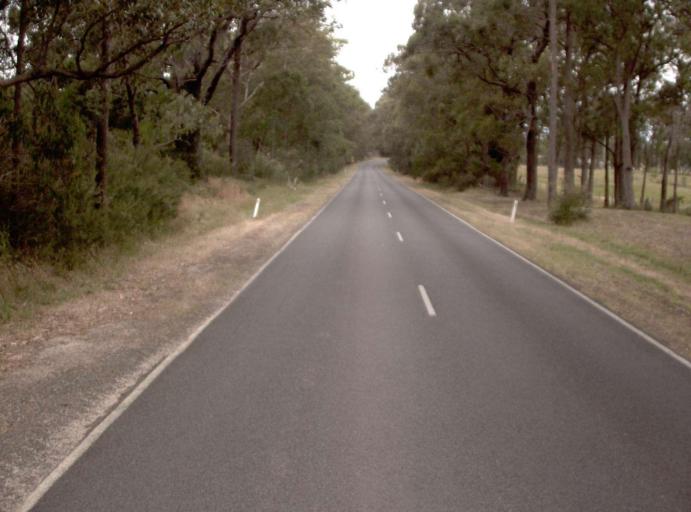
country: AU
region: Victoria
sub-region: Latrobe
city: Traralgon
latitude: -38.5122
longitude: 146.8530
